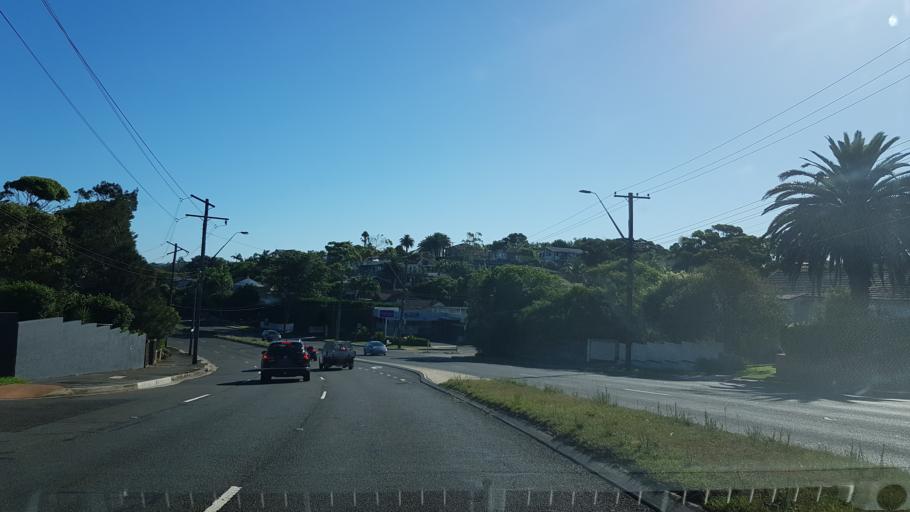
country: AU
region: New South Wales
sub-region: Pittwater
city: Newport
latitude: -33.6685
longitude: 151.3158
